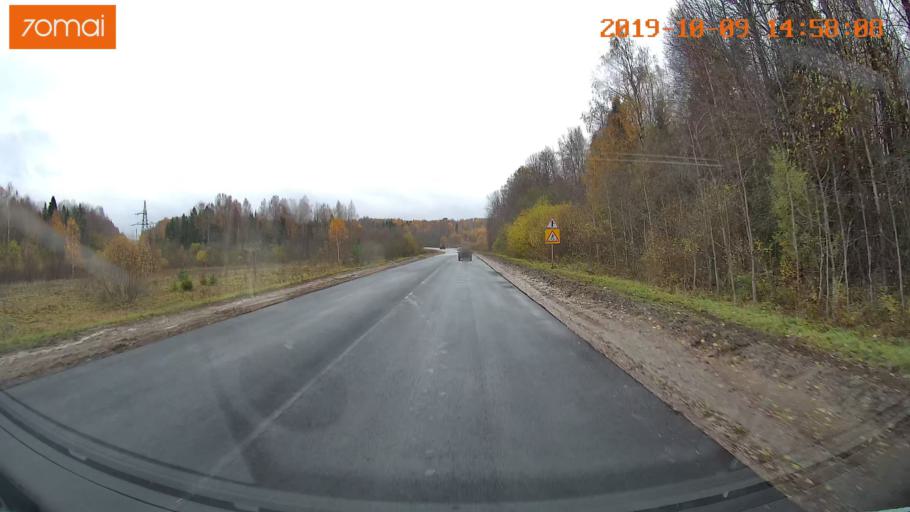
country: RU
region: Kostroma
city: Chistyye Bory
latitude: 58.3299
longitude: 41.6536
